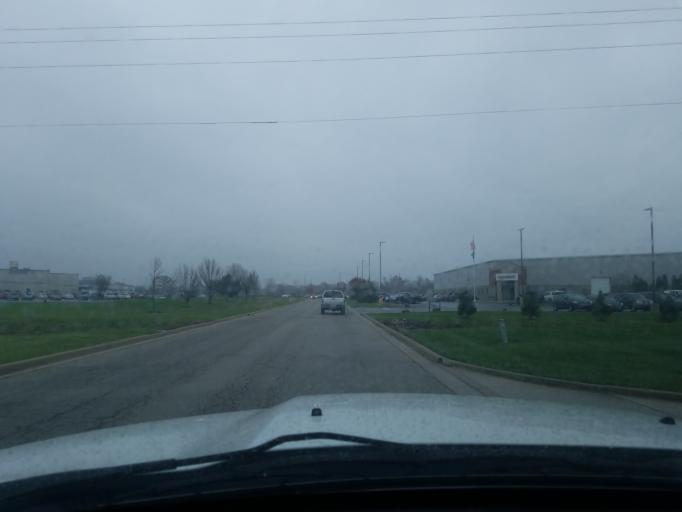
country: US
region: Indiana
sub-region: Delaware County
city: Muncie
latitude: 40.2307
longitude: -85.3946
